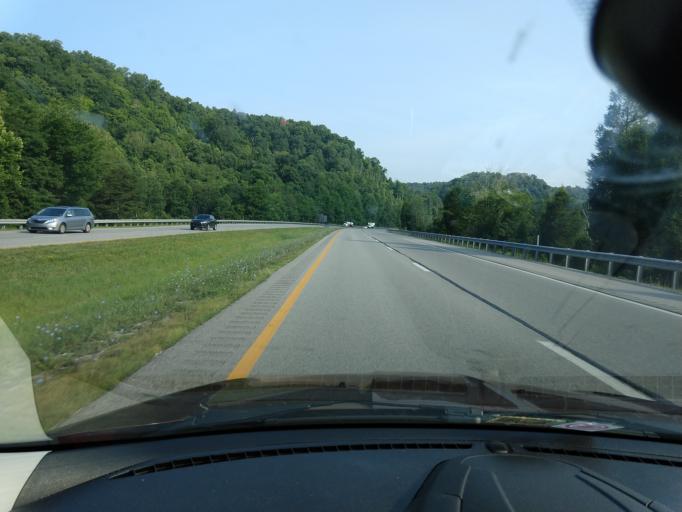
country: US
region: West Virginia
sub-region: Kanawha County
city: Sissonville
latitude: 38.5732
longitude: -81.6391
